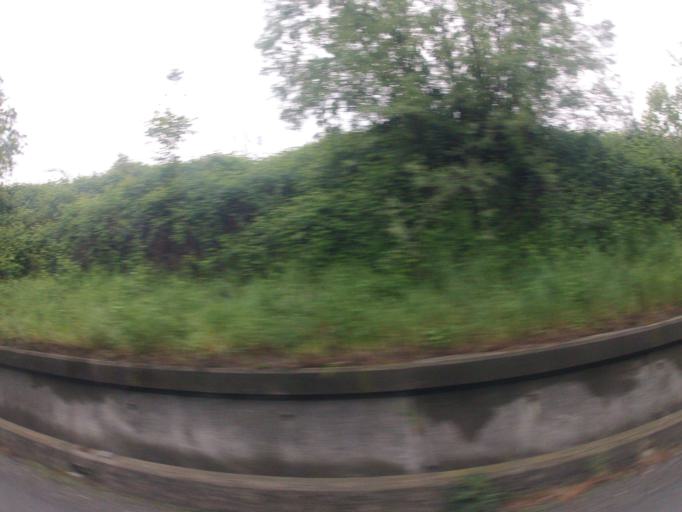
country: IT
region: Piedmont
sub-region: Provincia di Torino
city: La Loggia
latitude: 44.9443
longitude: 7.6770
